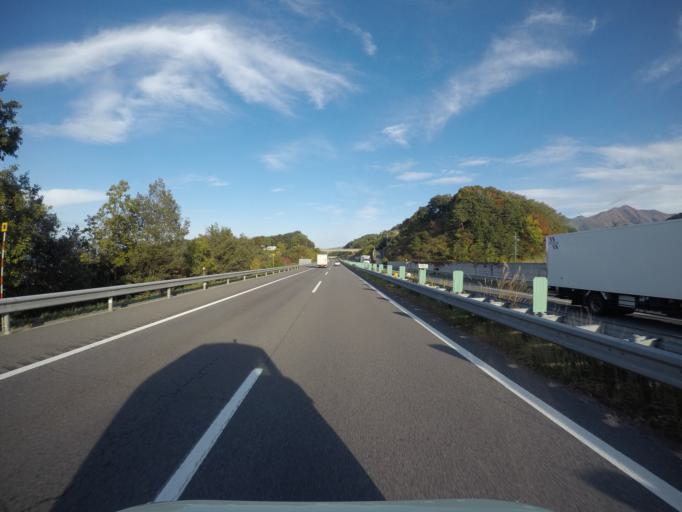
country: JP
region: Nagano
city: Komoro
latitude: 36.3353
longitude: 138.4436
